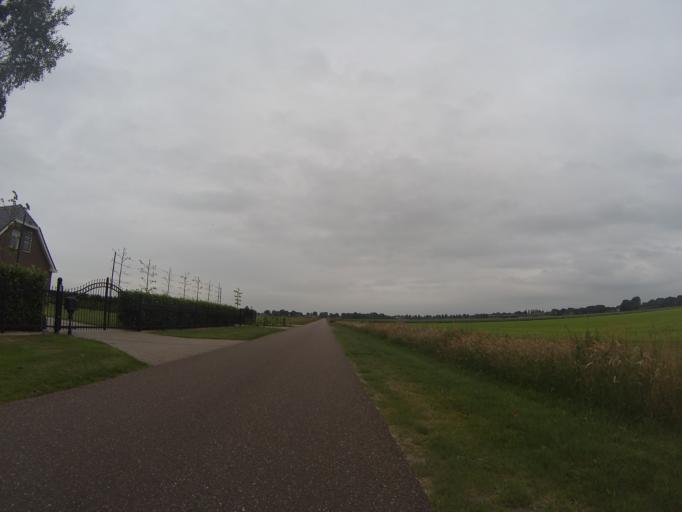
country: NL
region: Drenthe
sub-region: Gemeente Emmen
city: Emmer-Compascuum
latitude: 52.8044
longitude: 7.0253
